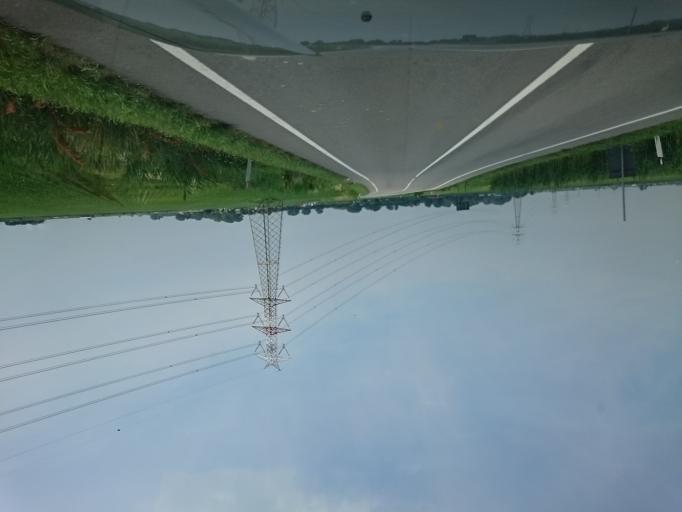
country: IT
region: Veneto
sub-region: Provincia di Padova
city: Codevigo
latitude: 45.2482
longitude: 12.1272
